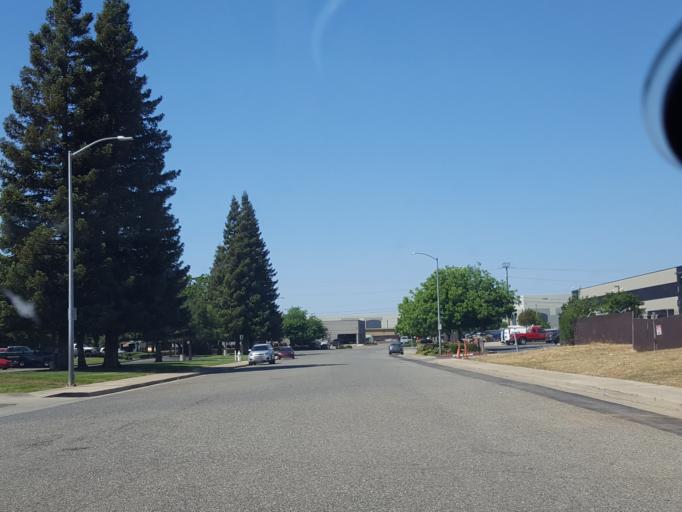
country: US
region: California
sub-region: Sacramento County
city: Rancho Cordova
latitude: 38.5882
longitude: -121.2620
